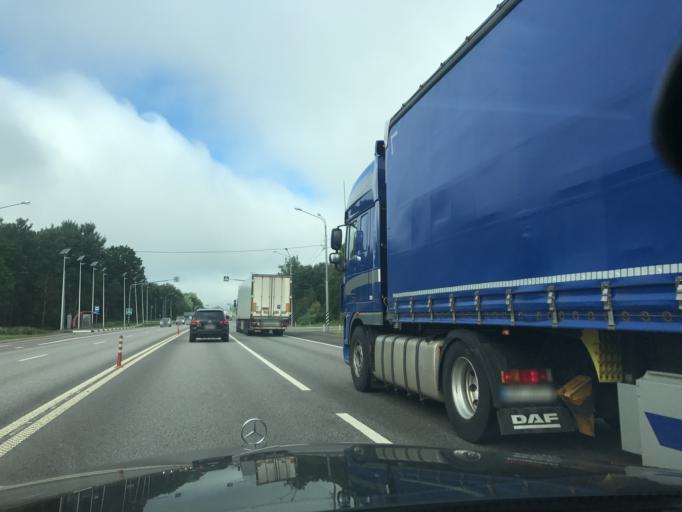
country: RU
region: Smolensk
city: Vyaz'ma
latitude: 55.2669
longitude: 34.3935
